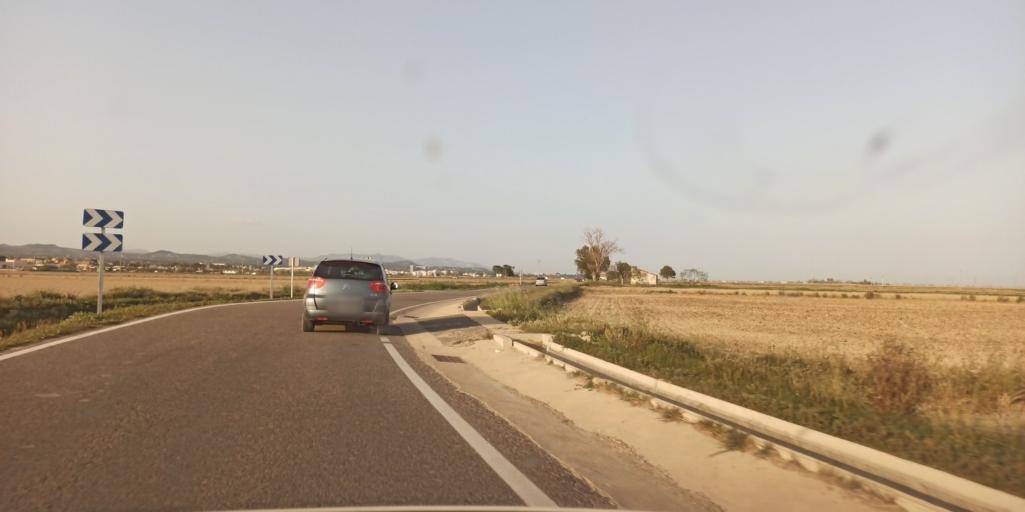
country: ES
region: Catalonia
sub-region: Provincia de Tarragona
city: L'Ampolla
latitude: 40.7872
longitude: 0.6935
